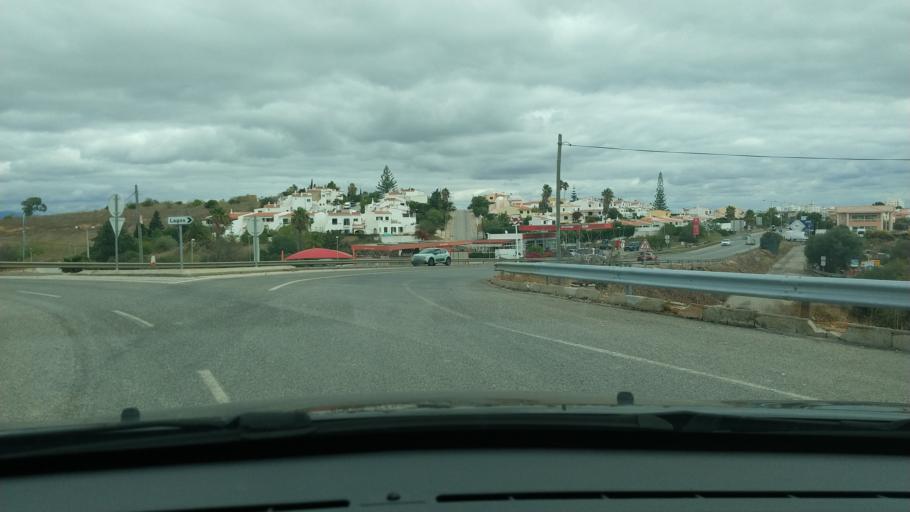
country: PT
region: Faro
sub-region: Lagos
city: Lagos
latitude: 37.1014
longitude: -8.6944
